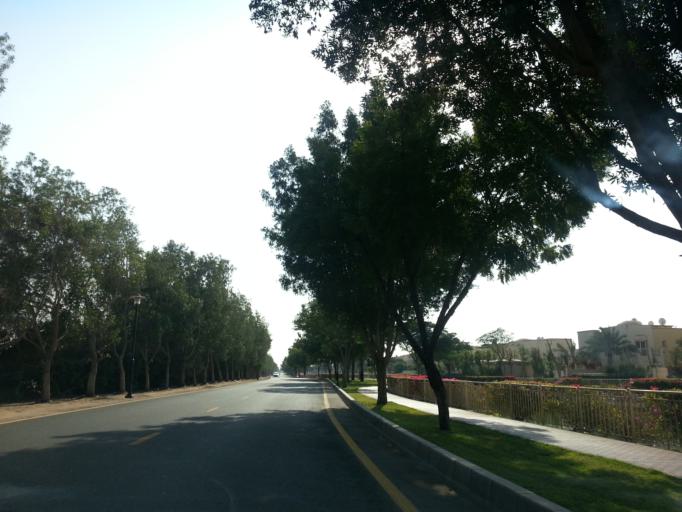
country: AE
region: Dubai
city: Dubai
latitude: 25.0625
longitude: 55.1923
